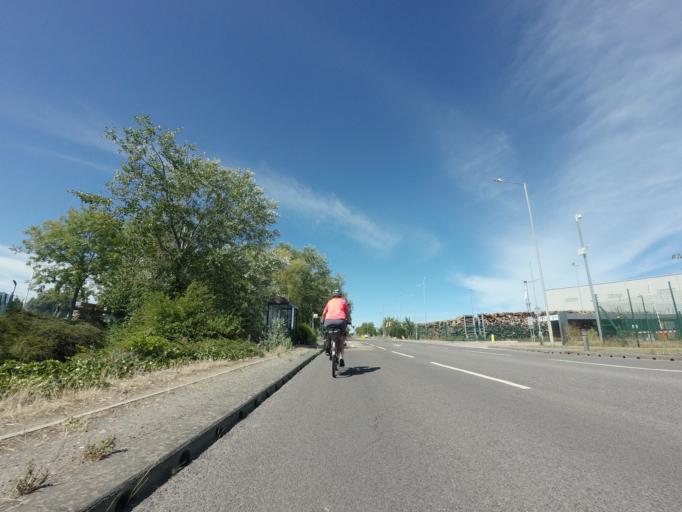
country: GB
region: England
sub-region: Kent
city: Sandwich
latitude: 51.2891
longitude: 1.3458
